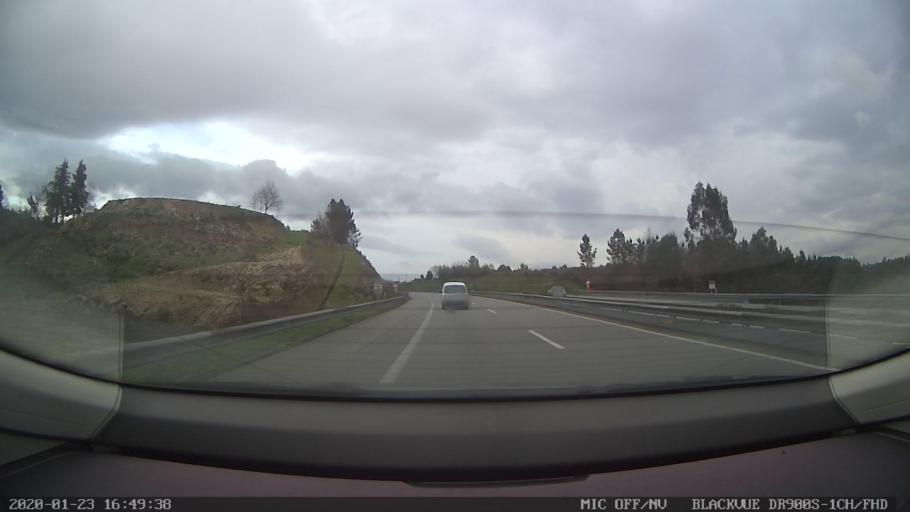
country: PT
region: Porto
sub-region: Marco de Canaveses
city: Marco de Canavezes
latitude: 41.2229
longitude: -8.1667
